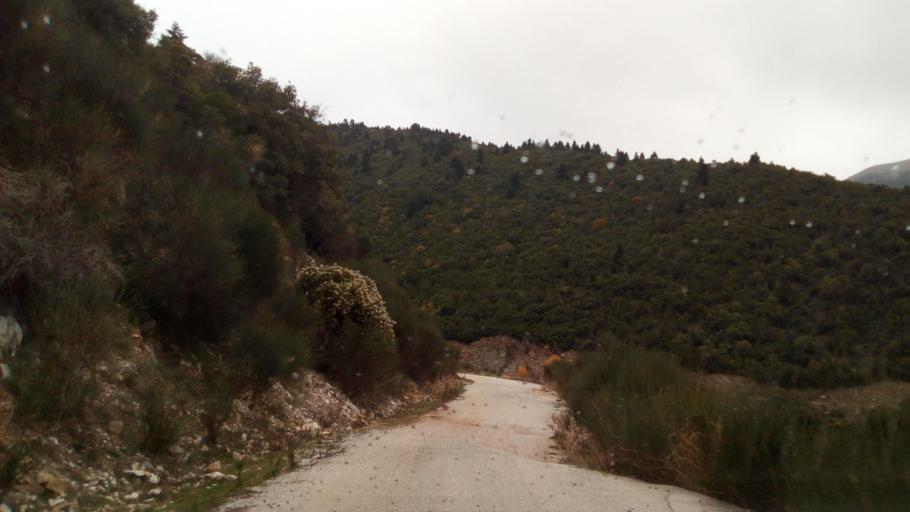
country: GR
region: West Greece
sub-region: Nomos Aitolias kai Akarnanias
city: Thermo
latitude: 38.6151
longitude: 21.8297
